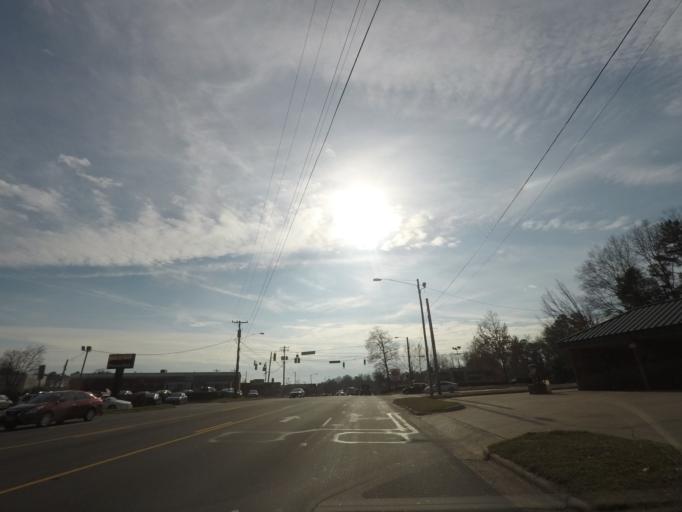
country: US
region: North Carolina
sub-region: Durham County
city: Durham
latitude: 36.0538
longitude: -78.9044
